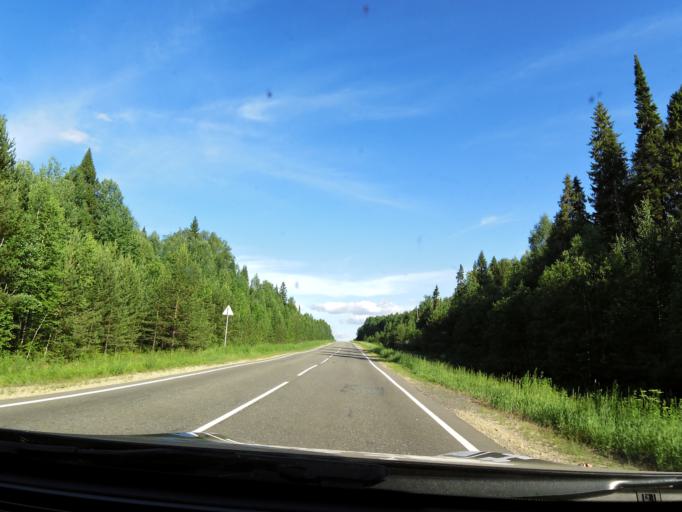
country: RU
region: Kirov
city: Chernaya Kholunitsa
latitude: 58.8197
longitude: 51.8119
